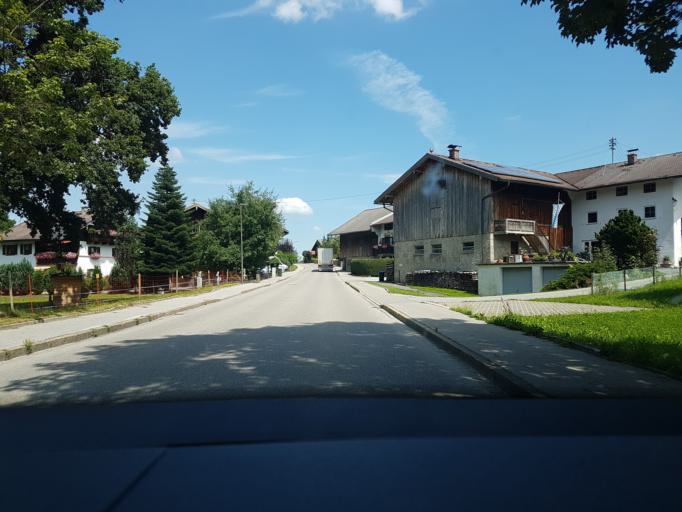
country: DE
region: Bavaria
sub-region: Upper Bavaria
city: Brannenburg
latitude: 47.7670
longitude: 12.0804
